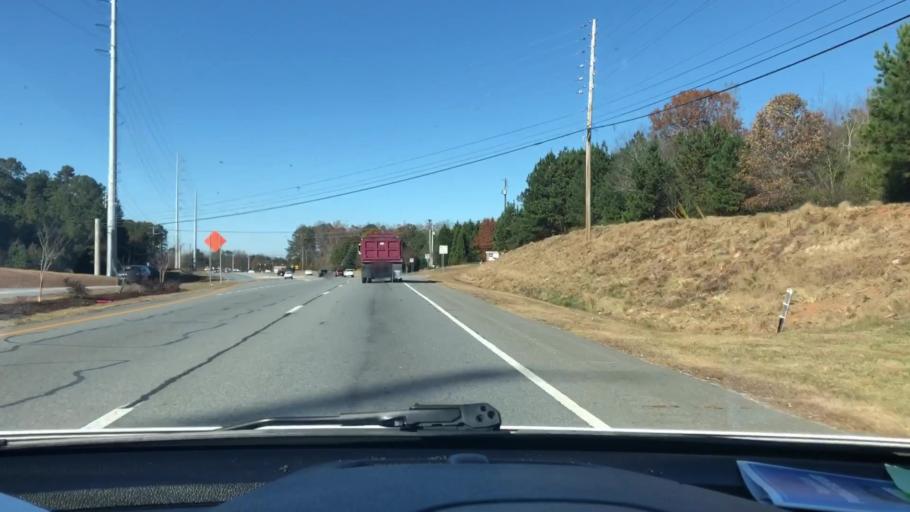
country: US
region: Georgia
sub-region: Forsyth County
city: Cumming
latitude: 34.1300
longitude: -84.1717
